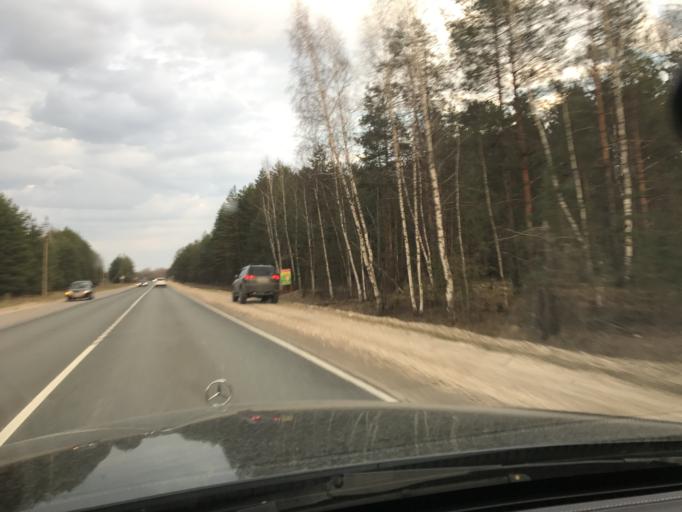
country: RU
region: Vladimir
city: Murom
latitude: 55.6214
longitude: 41.9102
